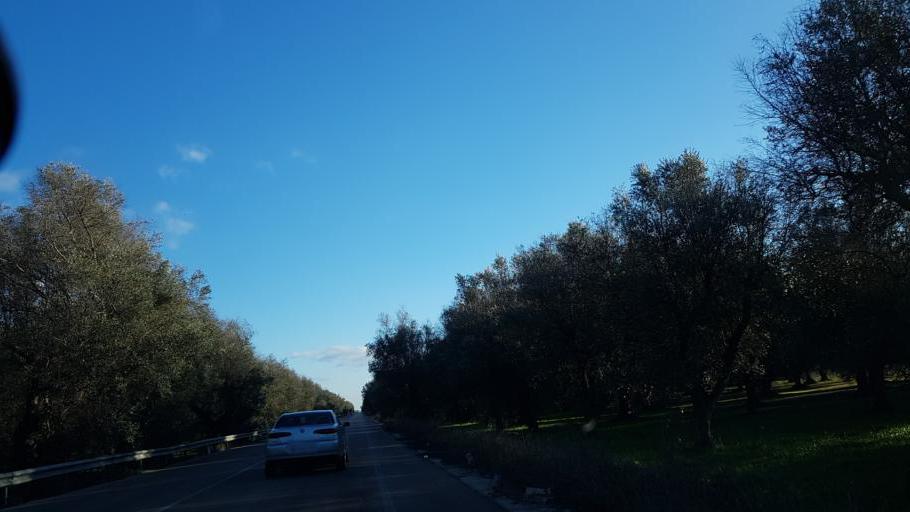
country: IT
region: Apulia
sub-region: Provincia di Brindisi
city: San Pietro Vernotico
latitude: 40.4699
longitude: 18.0134
